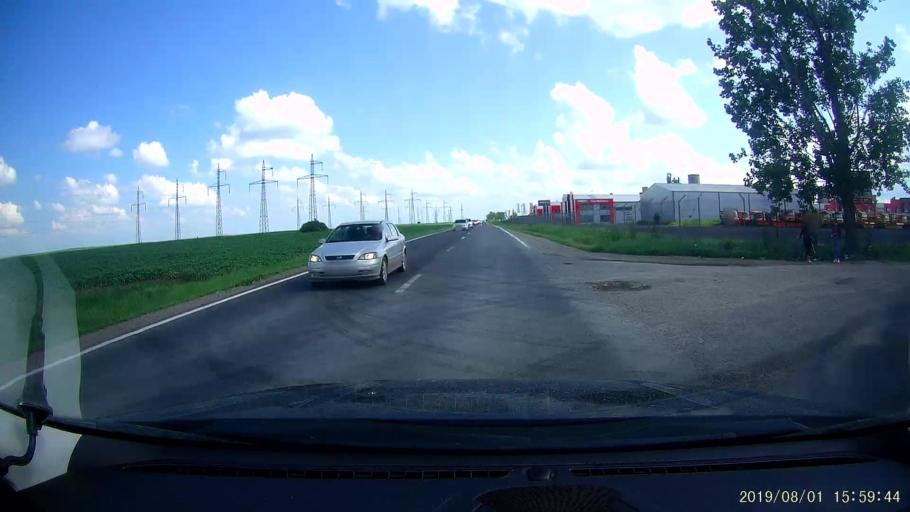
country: RO
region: Ialomita
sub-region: Comuna Slobozia
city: Slobozia
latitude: 44.5420
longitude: 27.3854
